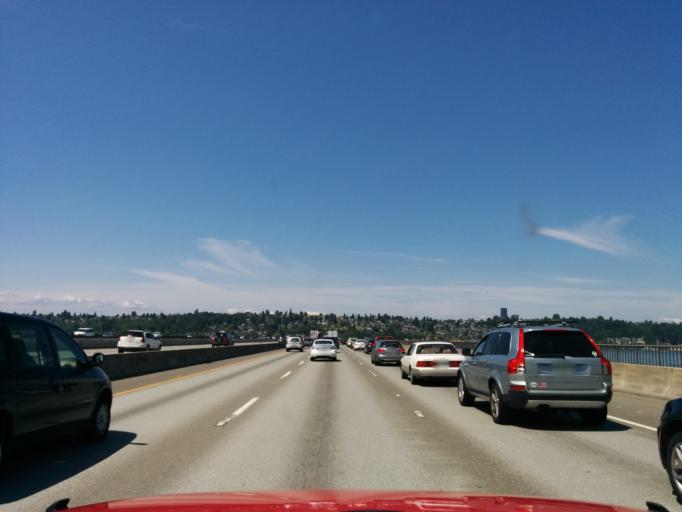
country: US
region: Washington
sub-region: King County
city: Mercer Island
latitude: 47.5897
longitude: -122.2629
